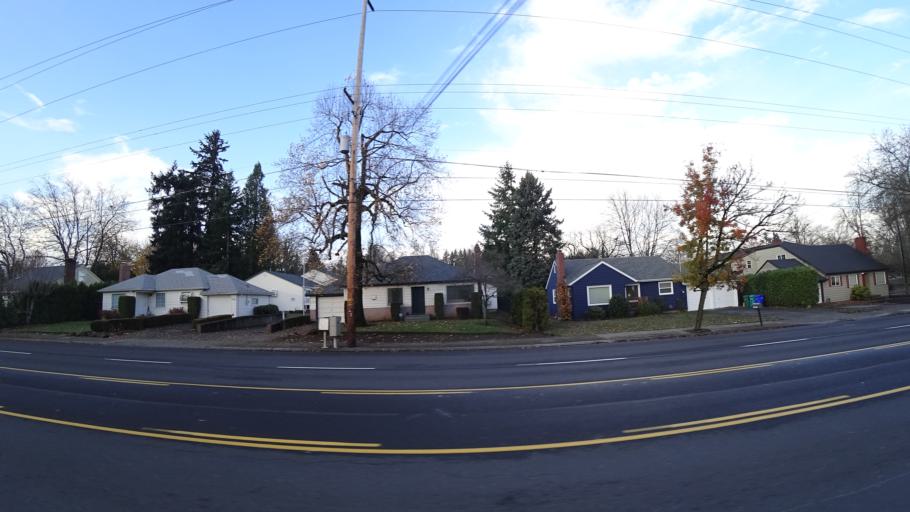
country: US
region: Oregon
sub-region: Multnomah County
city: Lents
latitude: 45.5189
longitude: -122.5476
